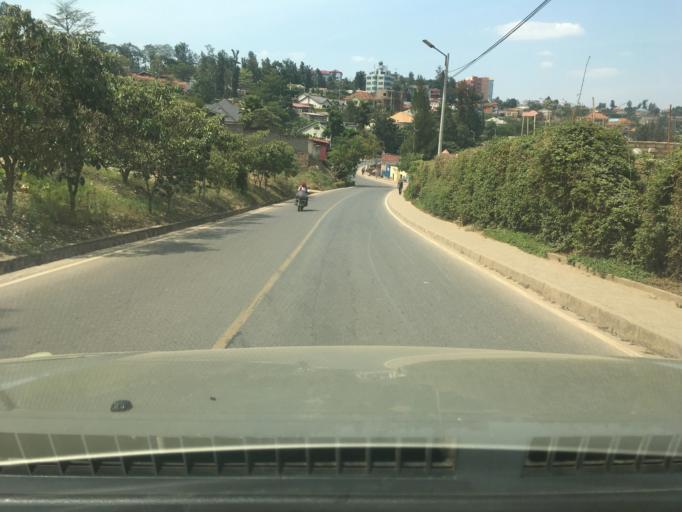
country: RW
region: Kigali
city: Kigali
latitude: -1.9542
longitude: 30.1005
